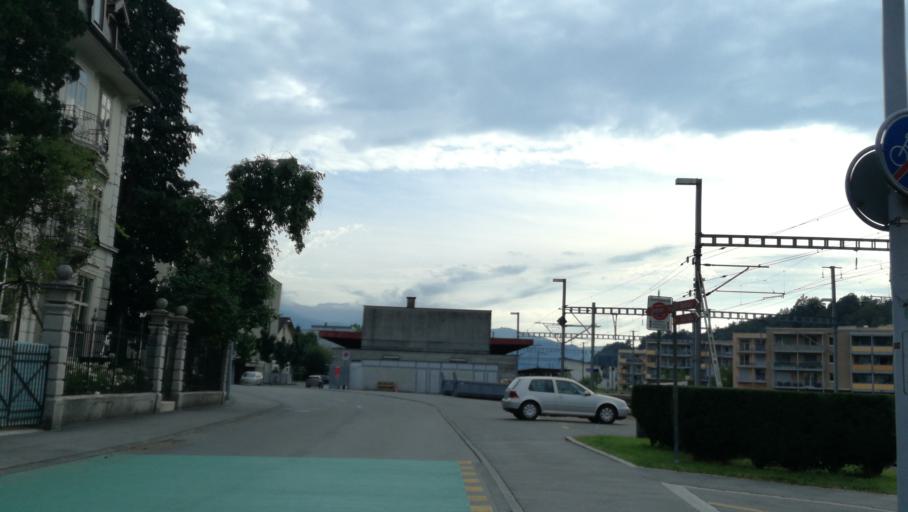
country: CH
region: Lucerne
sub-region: Lucerne-Land District
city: Ebikon
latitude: 47.0854
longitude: 8.3442
